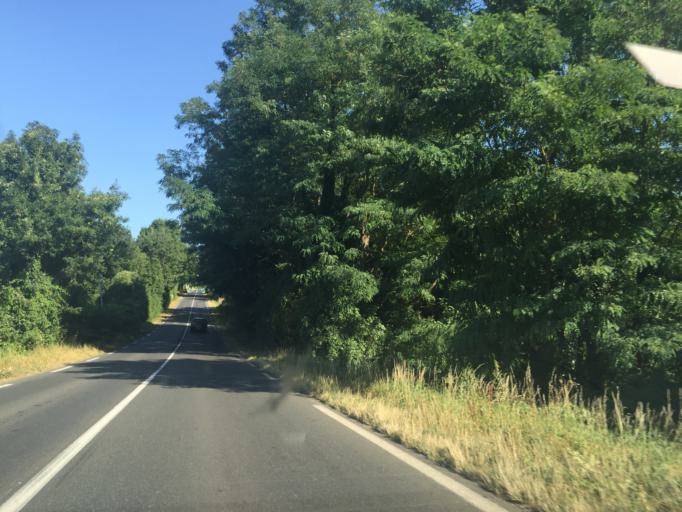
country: FR
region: Poitou-Charentes
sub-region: Departement des Deux-Sevres
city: Melle
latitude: 46.2185
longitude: -0.1297
